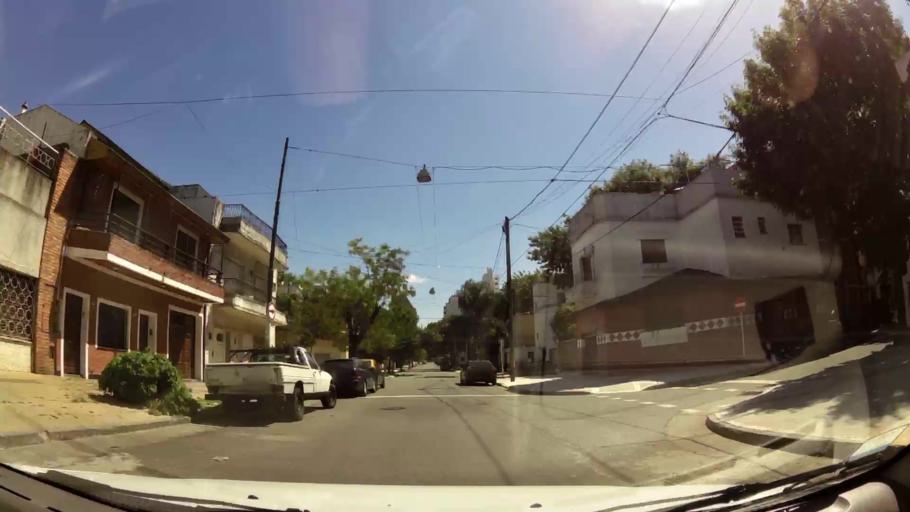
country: AR
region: Buenos Aires F.D.
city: Villa Santa Rita
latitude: -34.6323
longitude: -58.4378
